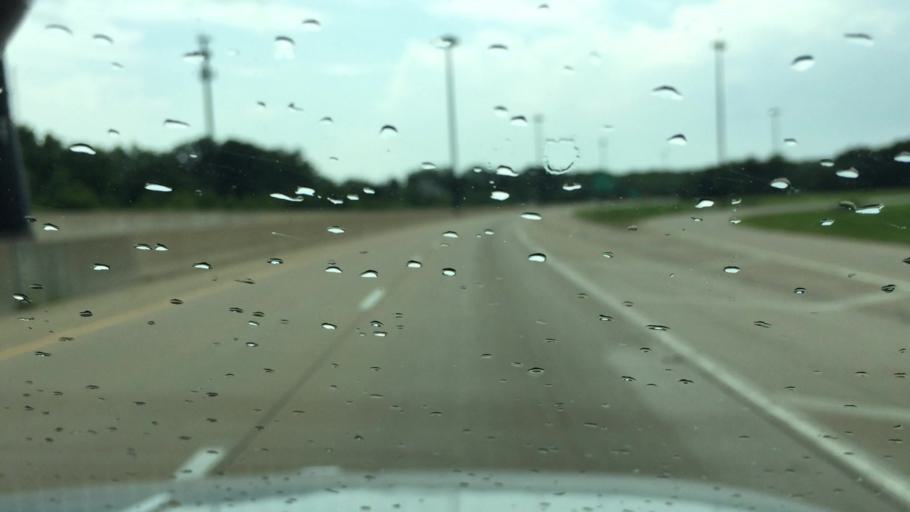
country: US
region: Illinois
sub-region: Peoria County
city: West Peoria
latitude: 40.7337
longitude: -89.6225
